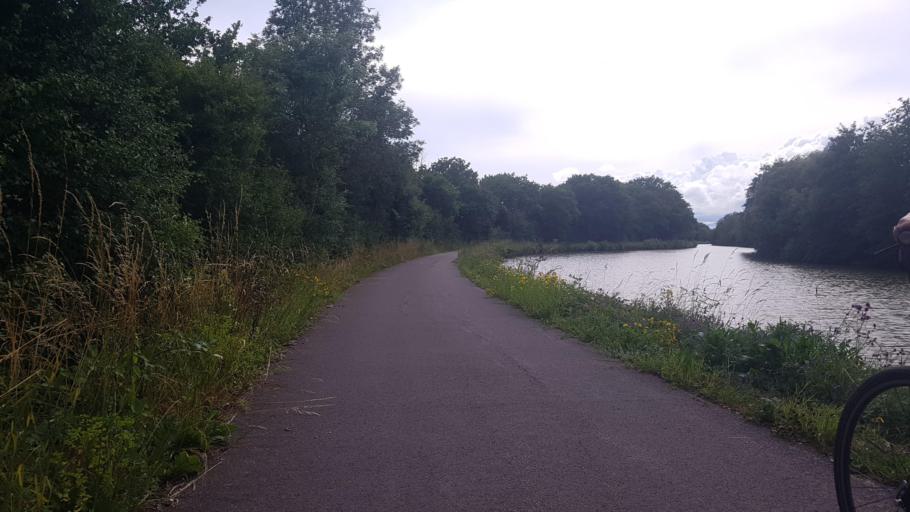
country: FR
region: Lorraine
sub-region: Departement de la Moselle
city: Dieuze
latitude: 48.6915
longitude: 6.7217
